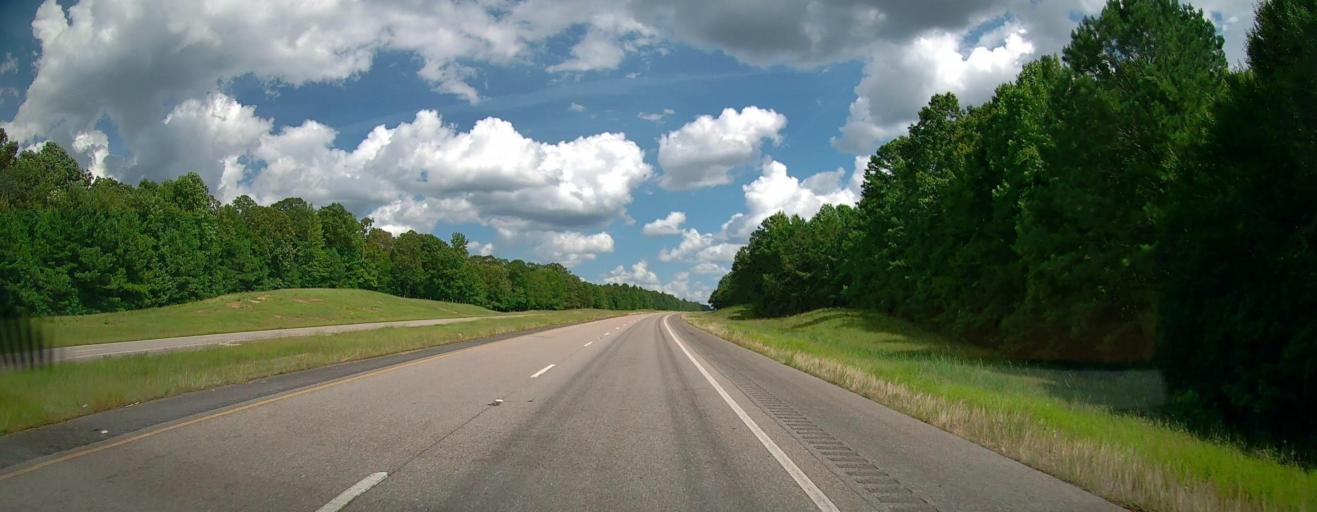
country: US
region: Mississippi
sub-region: Lowndes County
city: New Hope
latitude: 33.4665
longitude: -88.2323
